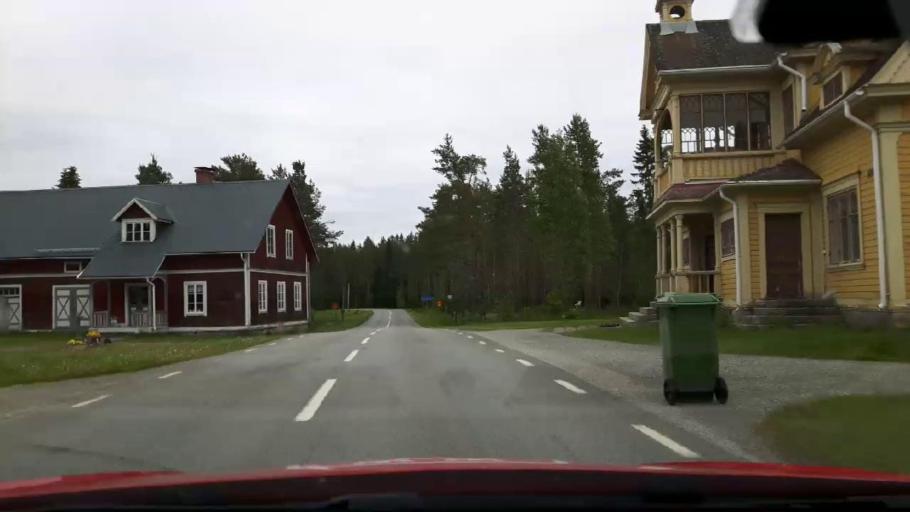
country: SE
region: Jaemtland
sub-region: Stroemsunds Kommun
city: Stroemsund
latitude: 63.4131
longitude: 15.6053
